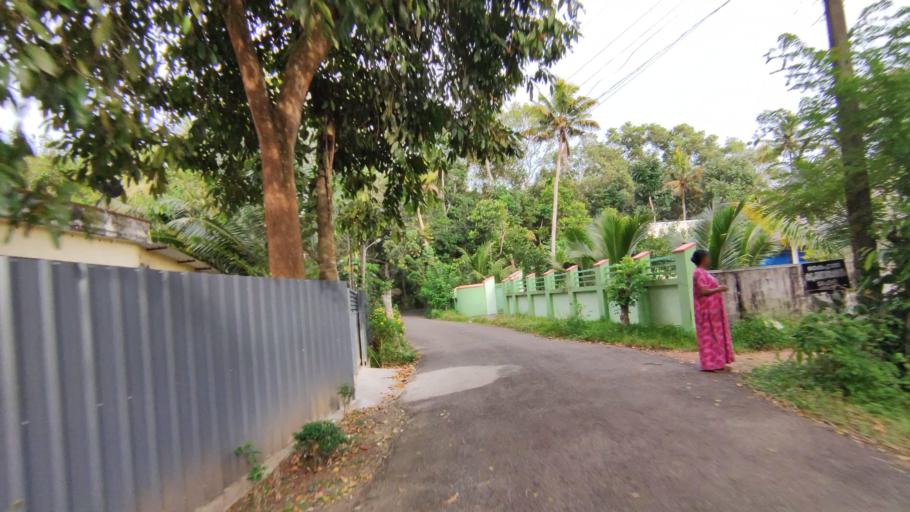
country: IN
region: Kerala
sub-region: Alappuzha
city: Shertallai
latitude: 9.6191
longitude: 76.3443
